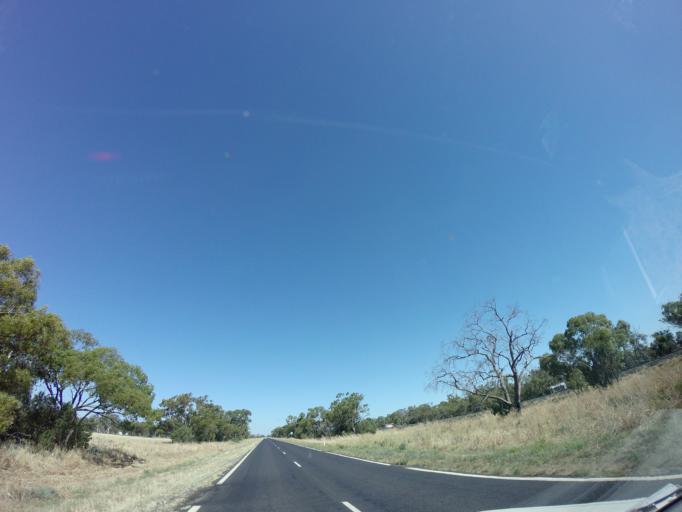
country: AU
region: New South Wales
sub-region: Bogan
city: Nyngan
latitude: -31.7726
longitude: 147.5940
